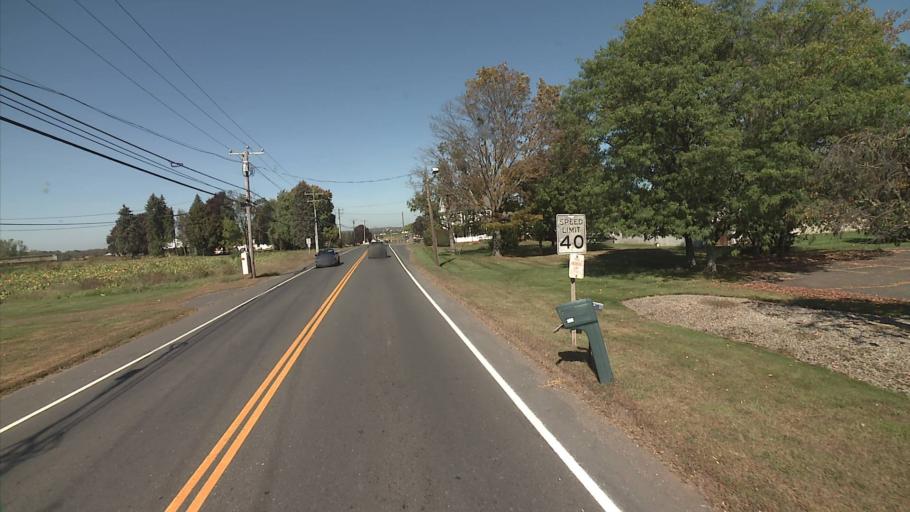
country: US
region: Connecticut
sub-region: Tolland County
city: Rockville
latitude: 41.8816
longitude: -72.4642
